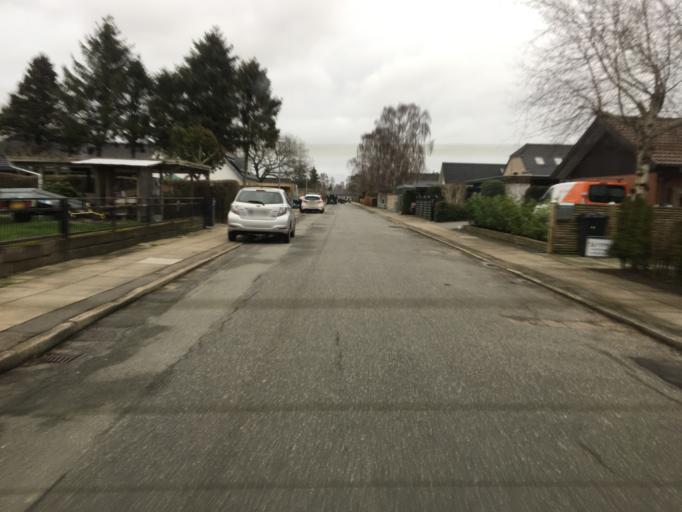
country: DK
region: Capital Region
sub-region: Tarnby Kommune
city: Tarnby
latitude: 55.6112
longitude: 12.5880
